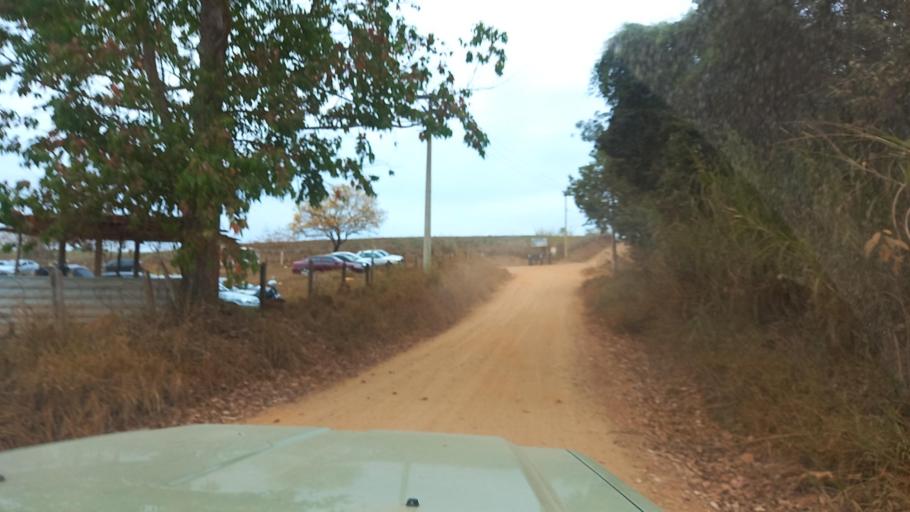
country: BR
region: Sao Paulo
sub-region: Moji-Guacu
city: Mogi-Gaucu
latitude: -22.3102
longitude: -46.8358
